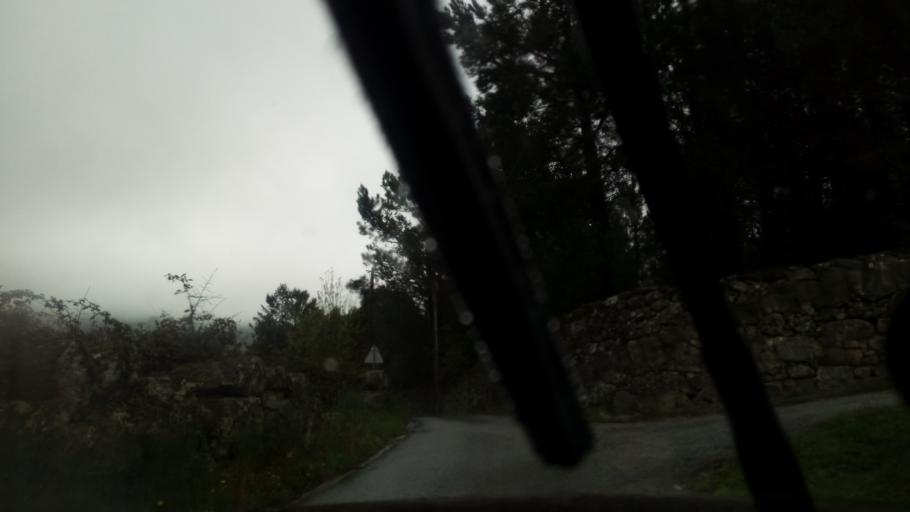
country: PT
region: Guarda
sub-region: Fornos de Algodres
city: Fornos de Algodres
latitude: 40.6196
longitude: -7.5288
